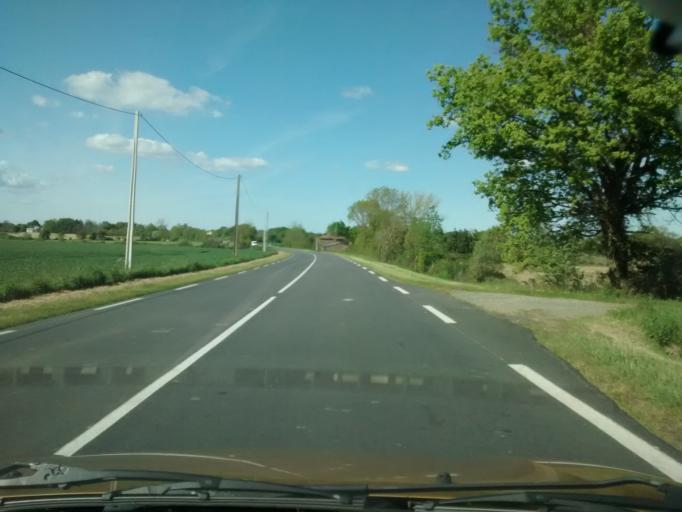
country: FR
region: Pays de la Loire
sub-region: Departement de la Vendee
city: Saint-Philbert-de-Bouaine
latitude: 47.0113
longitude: -1.5045
